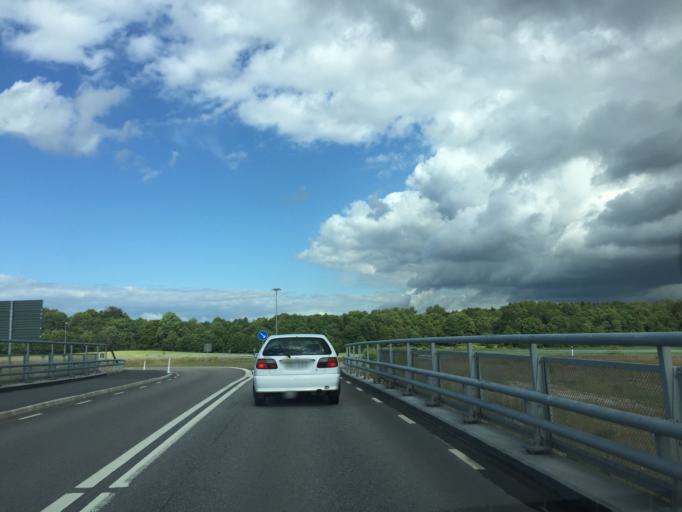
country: SE
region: OEstergoetland
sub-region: Motala Kommun
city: Motala
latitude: 58.5080
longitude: 15.0261
